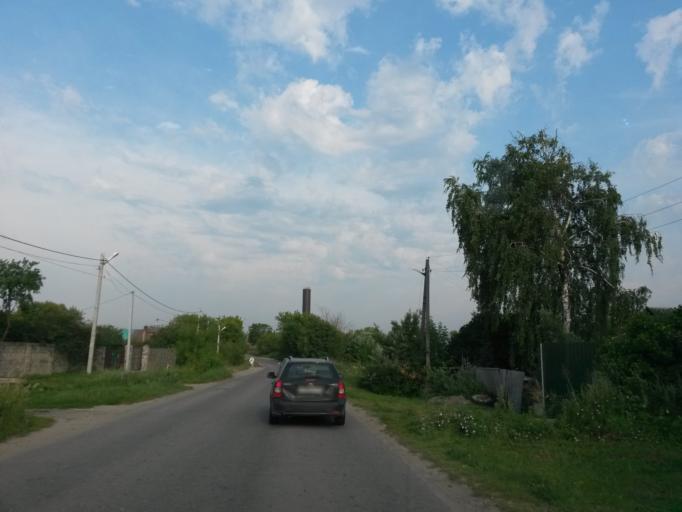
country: RU
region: Moskovskaya
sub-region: Podol'skiy Rayon
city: Podol'sk
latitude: 55.4467
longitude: 37.6268
